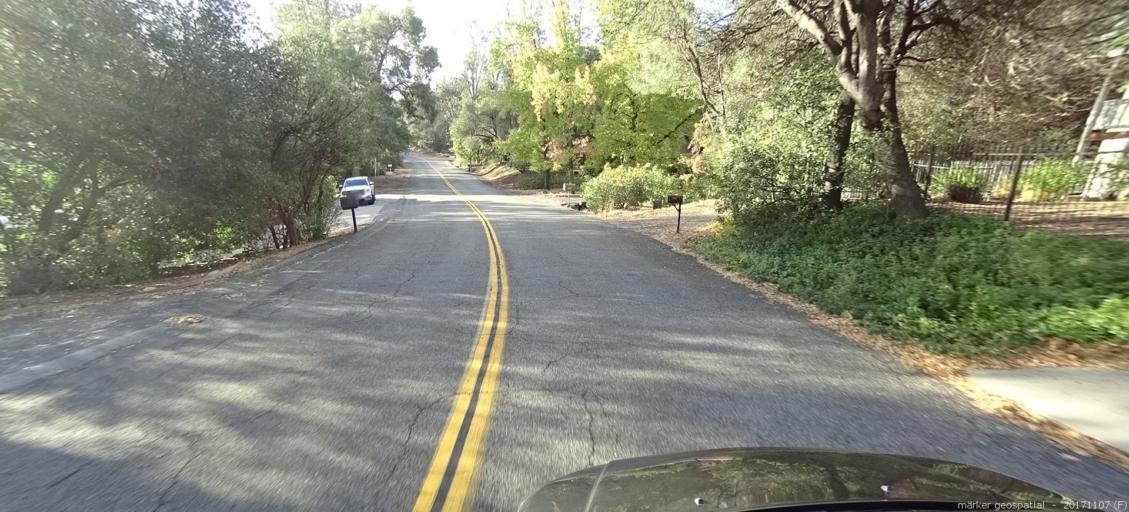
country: US
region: California
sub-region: Shasta County
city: Shasta
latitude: 40.5845
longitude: -122.4672
